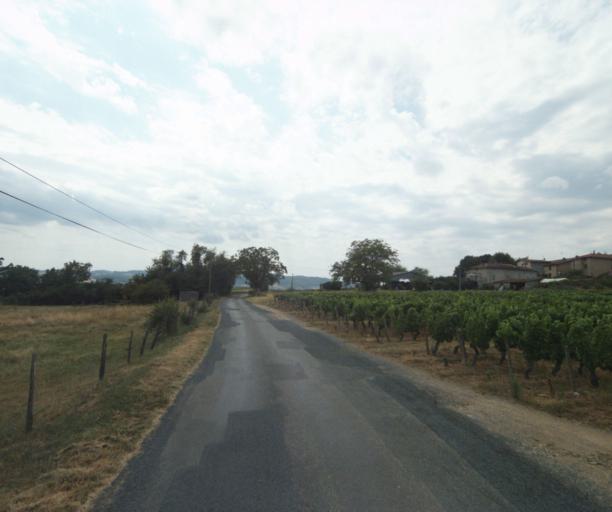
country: FR
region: Rhone-Alpes
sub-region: Departement du Rhone
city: Bully
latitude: 45.8690
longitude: 4.5863
